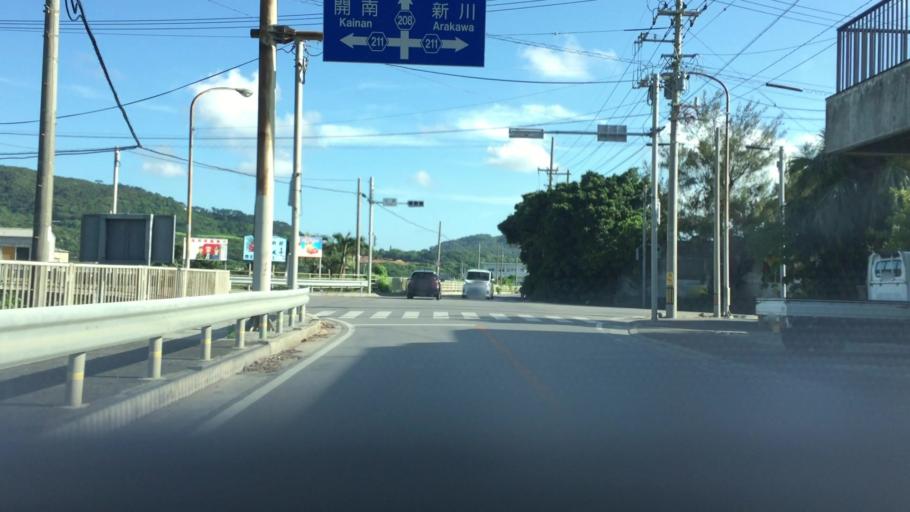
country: JP
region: Okinawa
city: Ishigaki
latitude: 24.3954
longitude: 124.1563
